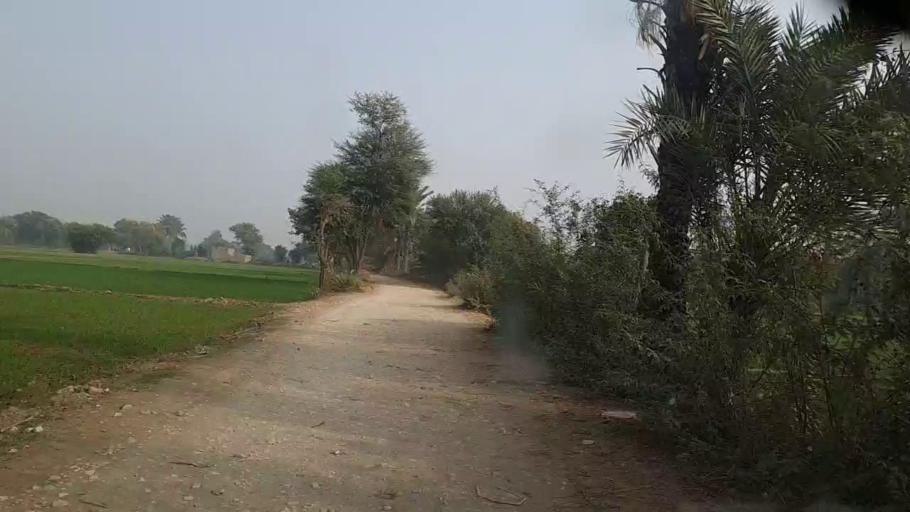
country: PK
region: Sindh
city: Bozdar
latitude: 27.1333
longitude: 68.6570
